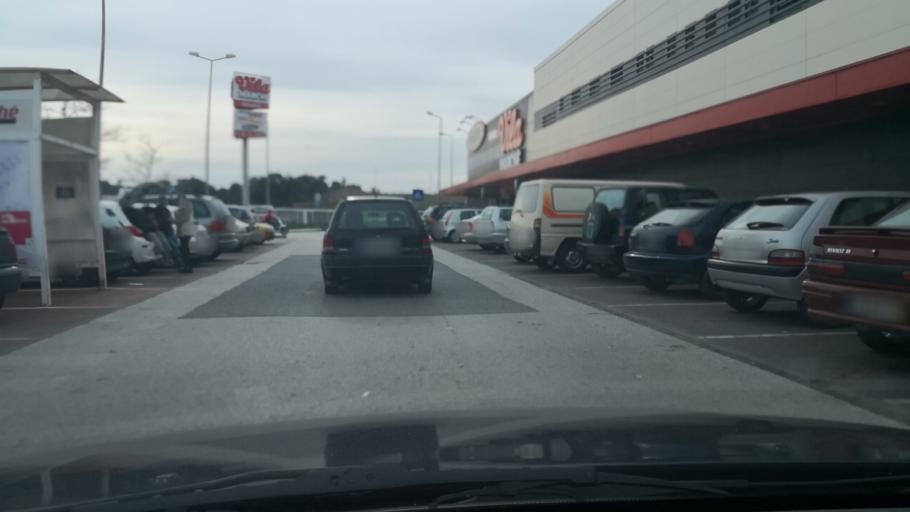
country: PT
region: Setubal
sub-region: Setubal
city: Setubal
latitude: 38.5379
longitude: -8.8573
